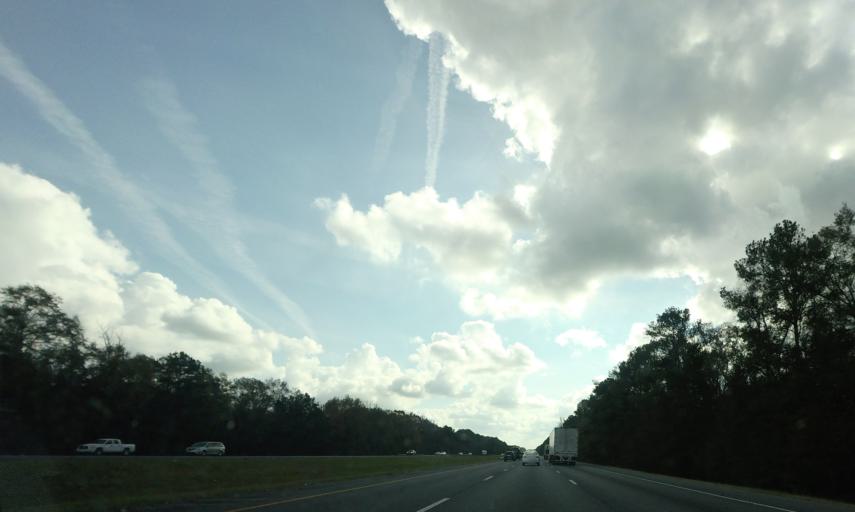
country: US
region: Georgia
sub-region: Houston County
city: Perry
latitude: 32.3754
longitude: -83.7684
